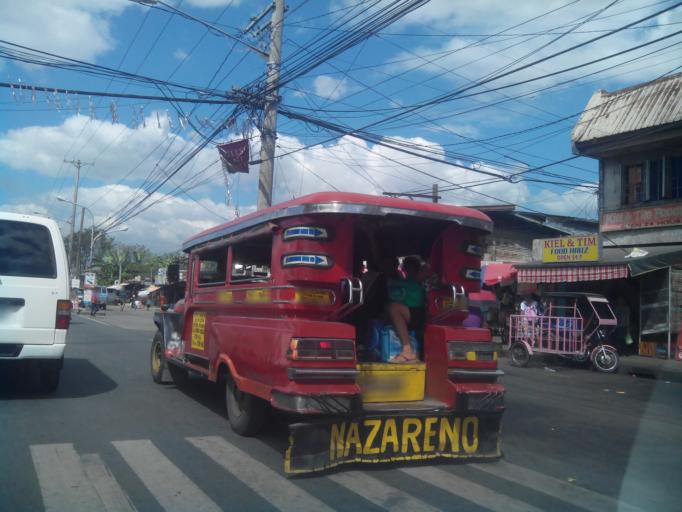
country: PH
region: Calabarzon
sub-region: Province of Rizal
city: Taytay
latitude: 14.5439
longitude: 121.1443
